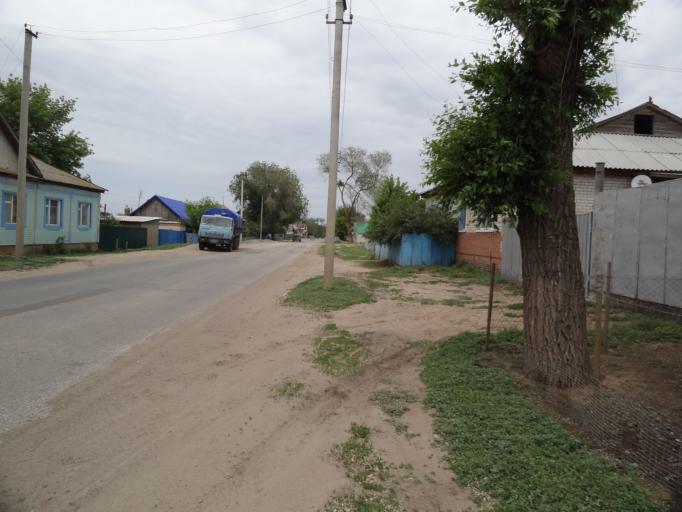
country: RU
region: Saratov
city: Privolzhskiy
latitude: 51.1822
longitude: 45.9191
